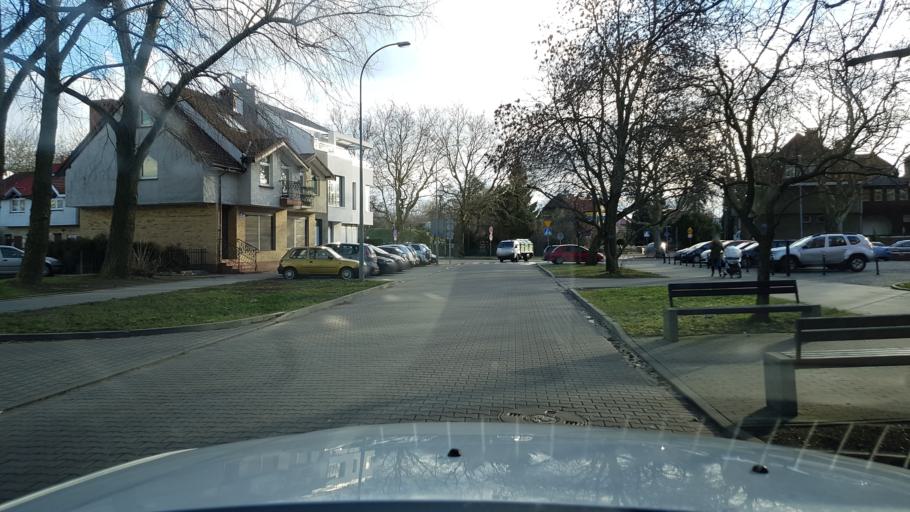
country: PL
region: West Pomeranian Voivodeship
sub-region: Powiat kolobrzeski
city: Kolobrzeg
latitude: 54.1741
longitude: 15.5646
